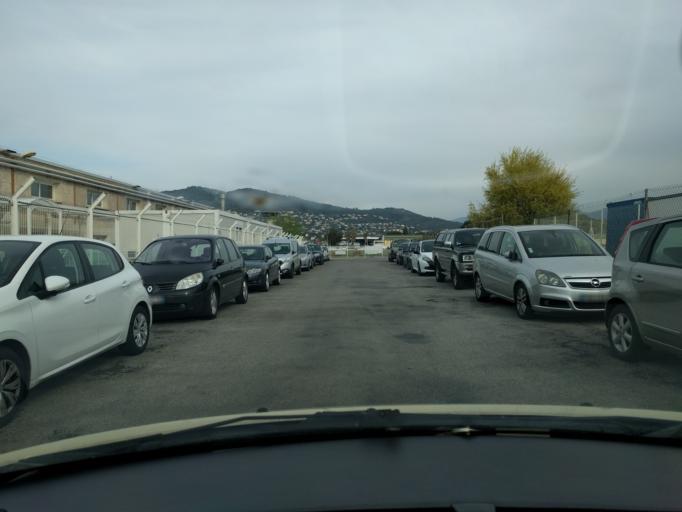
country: FR
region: Provence-Alpes-Cote d'Azur
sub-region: Departement des Alpes-Maritimes
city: Mandelieu-la-Napoule
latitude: 43.5444
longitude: 6.9577
